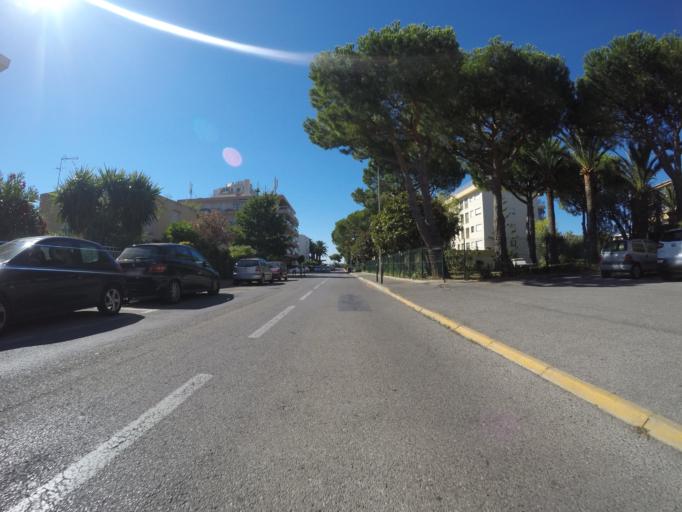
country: FR
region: Provence-Alpes-Cote d'Azur
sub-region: Departement des Alpes-Maritimes
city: Saint-Laurent-du-Var
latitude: 43.6585
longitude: 7.1801
